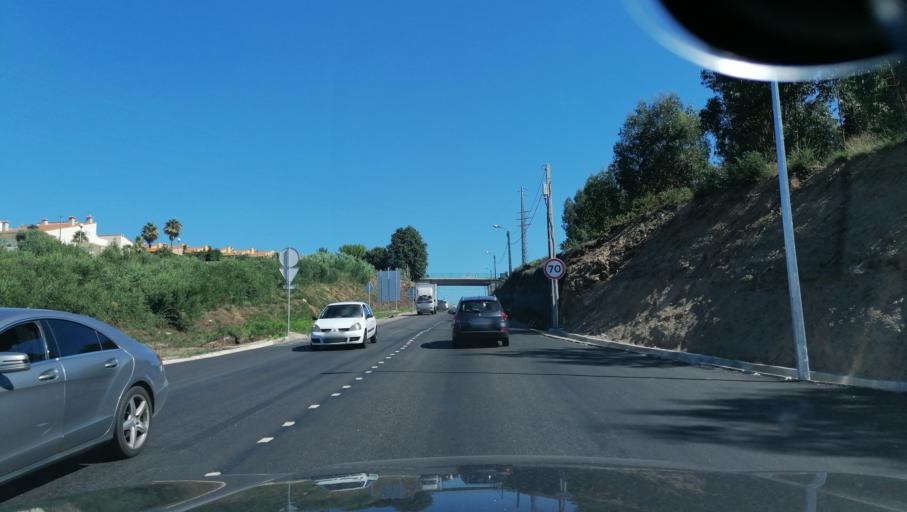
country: PT
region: Aveiro
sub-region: Santa Maria da Feira
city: Arrifana
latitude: 40.9288
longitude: -8.5110
